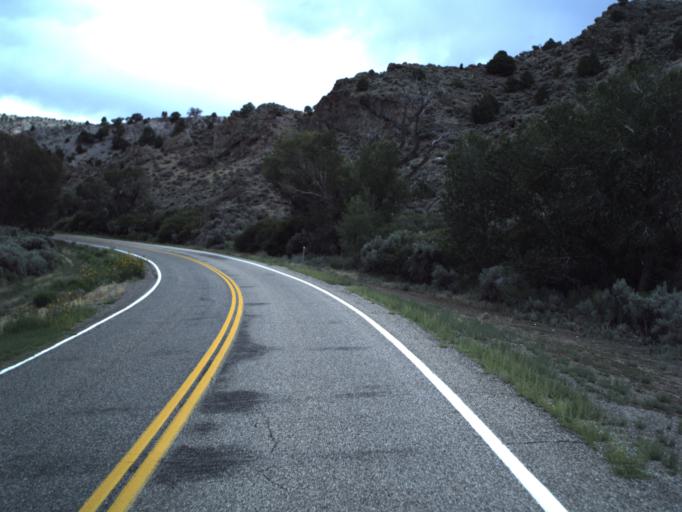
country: US
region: Utah
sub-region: Piute County
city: Junction
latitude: 38.2007
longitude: -112.1669
